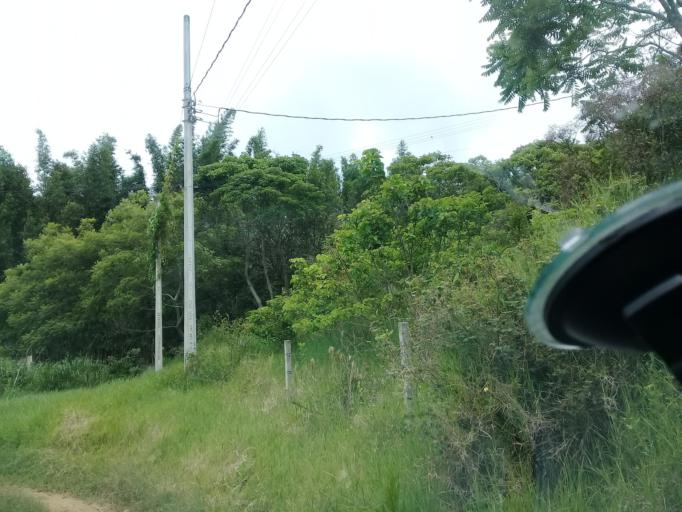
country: MX
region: Veracruz
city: El Castillo
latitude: 19.5344
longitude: -96.8846
